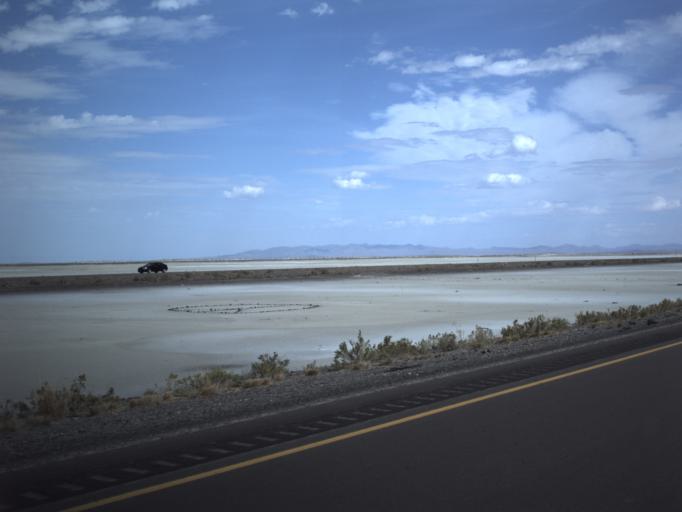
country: US
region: Utah
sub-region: Tooele County
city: Wendover
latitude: 40.7300
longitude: -113.4619
